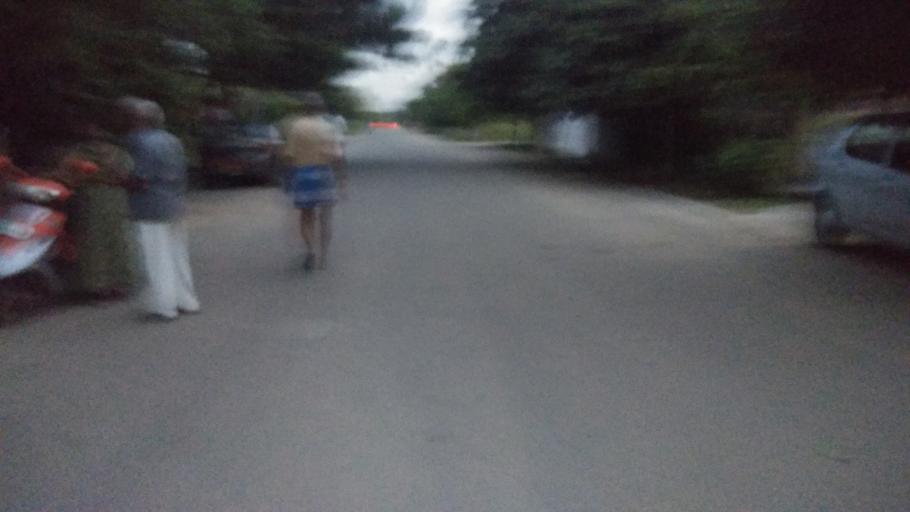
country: IN
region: Tamil Nadu
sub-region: Thiruvallur
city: Tiruvallur
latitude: 13.1215
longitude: 79.9226
